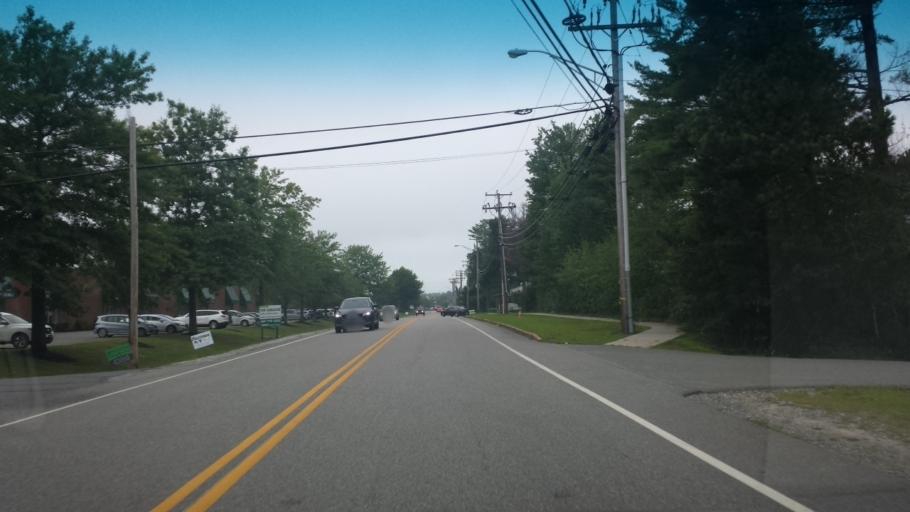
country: US
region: Maine
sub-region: Cumberland County
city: South Portland Gardens
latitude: 43.6292
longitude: -70.3273
